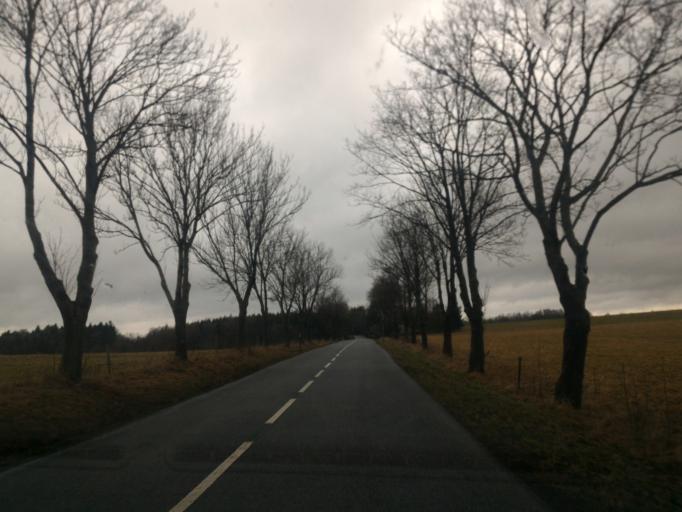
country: CZ
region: Ustecky
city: Stare Krecany
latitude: 50.9270
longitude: 14.4832
